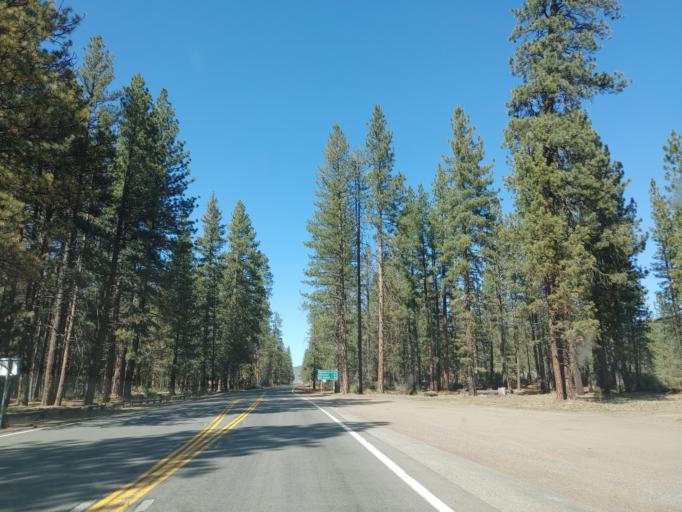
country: US
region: California
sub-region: Shasta County
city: Burney
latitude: 40.6810
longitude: -121.4245
